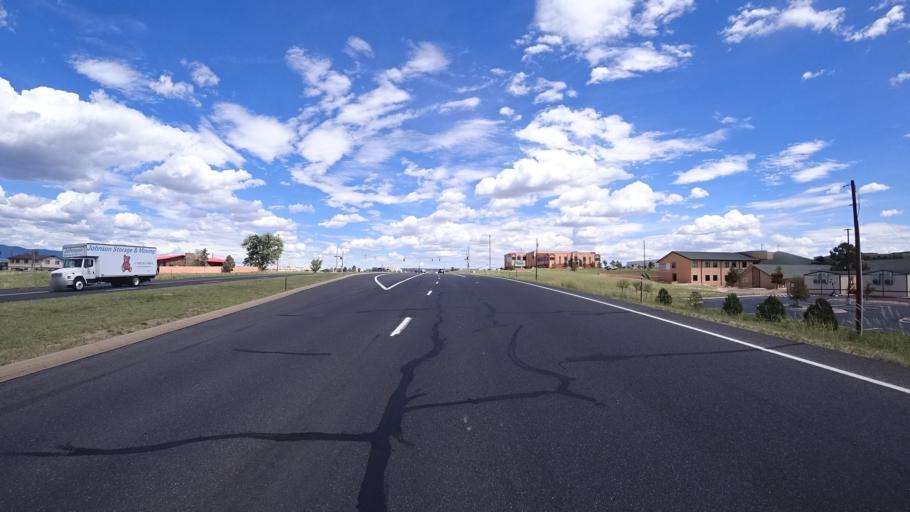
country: US
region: Colorado
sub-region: El Paso County
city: Air Force Academy
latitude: 38.9790
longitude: -104.7977
